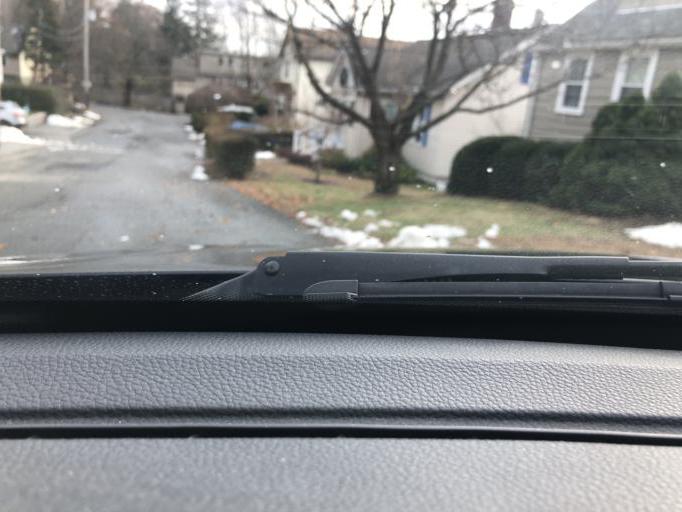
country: US
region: Massachusetts
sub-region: Middlesex County
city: Arlington
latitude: 42.4255
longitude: -71.1674
